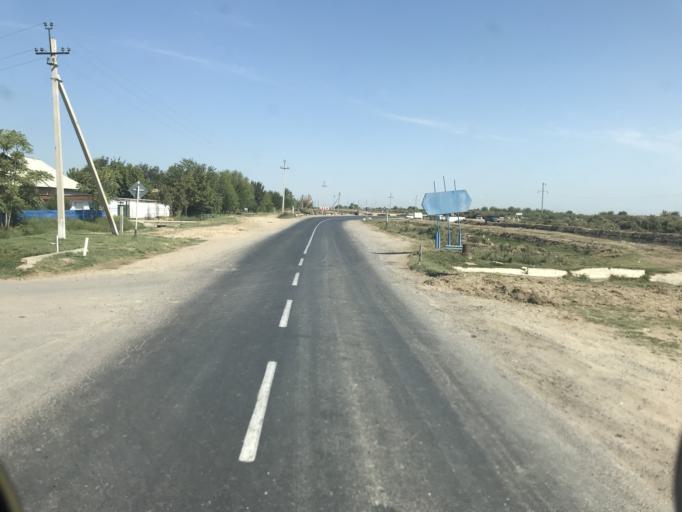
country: KZ
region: Ongtustik Qazaqstan
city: Myrzakent
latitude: 40.7153
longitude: 68.5337
